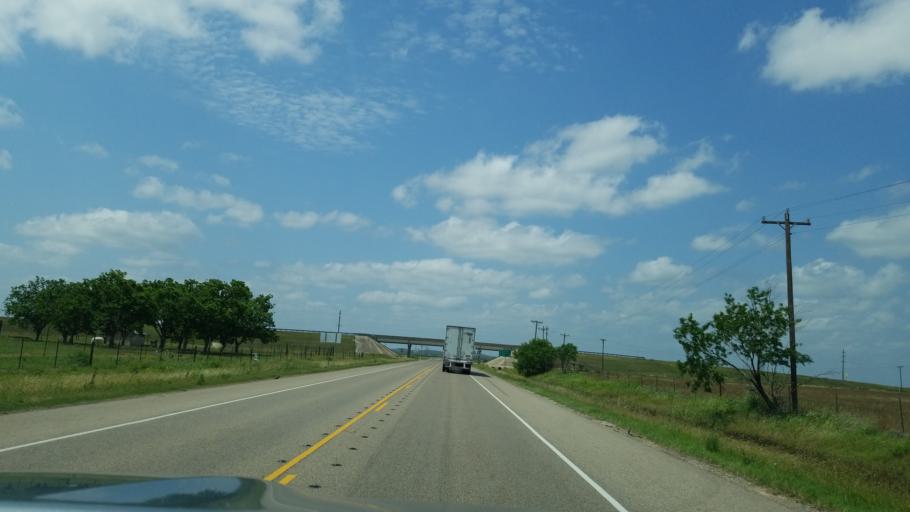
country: US
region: Texas
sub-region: Frio County
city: Pearsall
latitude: 28.9743
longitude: -99.2407
